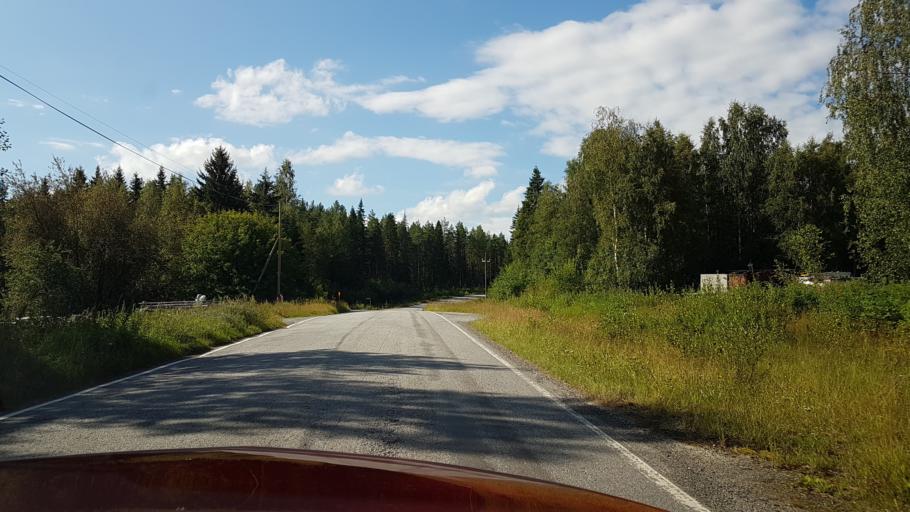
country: FI
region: Northern Ostrobothnia
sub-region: Ylivieska
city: Himanka
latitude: 64.0912
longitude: 23.7631
